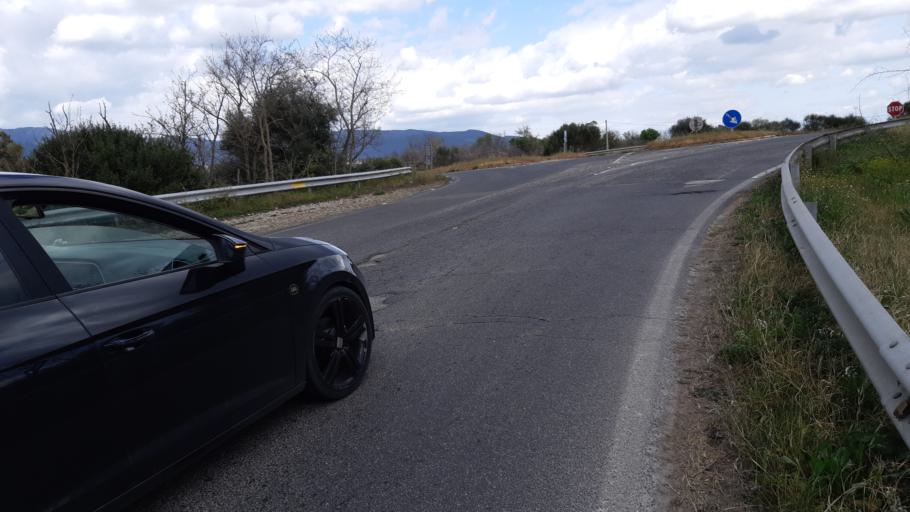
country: IT
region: Sardinia
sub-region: Provincia di Carbonia-Iglesias
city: Domusnovas
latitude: 39.3135
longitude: 8.6437
